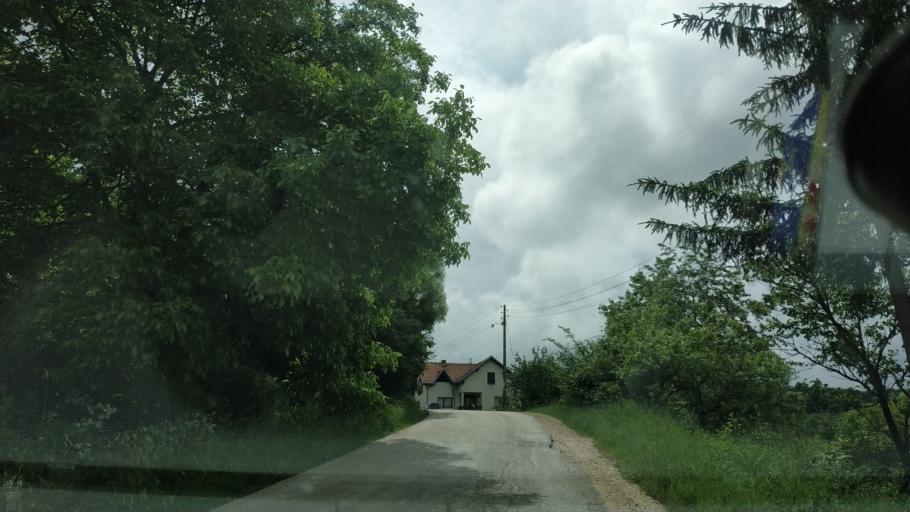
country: RS
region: Central Serbia
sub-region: Zajecarski Okrug
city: Soko Banja
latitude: 43.6800
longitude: 21.9245
